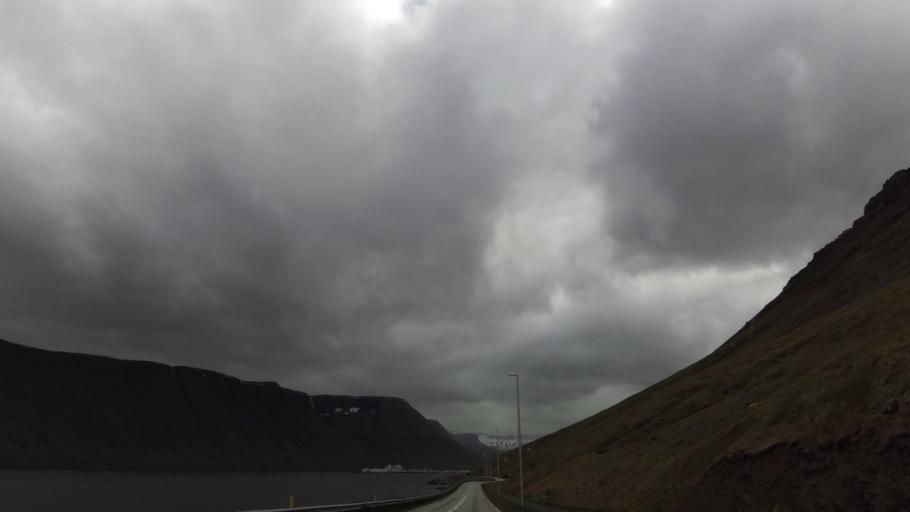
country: IS
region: Westfjords
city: Isafjoerdur
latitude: 66.0979
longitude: -23.1106
